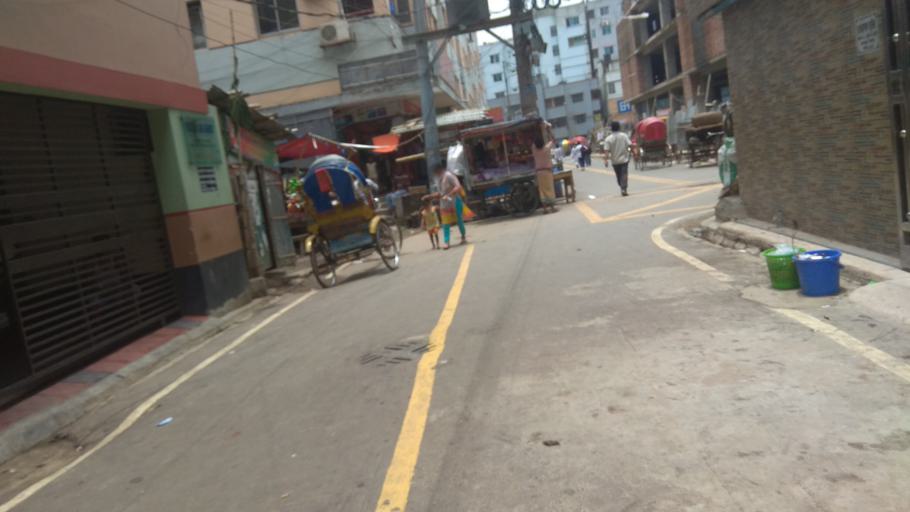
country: BD
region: Dhaka
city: Tungi
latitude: 23.8153
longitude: 90.3568
